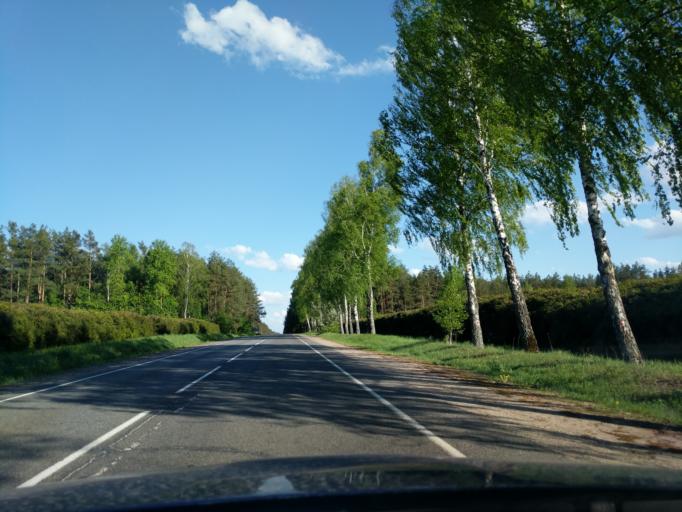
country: BY
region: Minsk
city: Myadzyel
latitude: 54.8270
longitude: 26.9442
